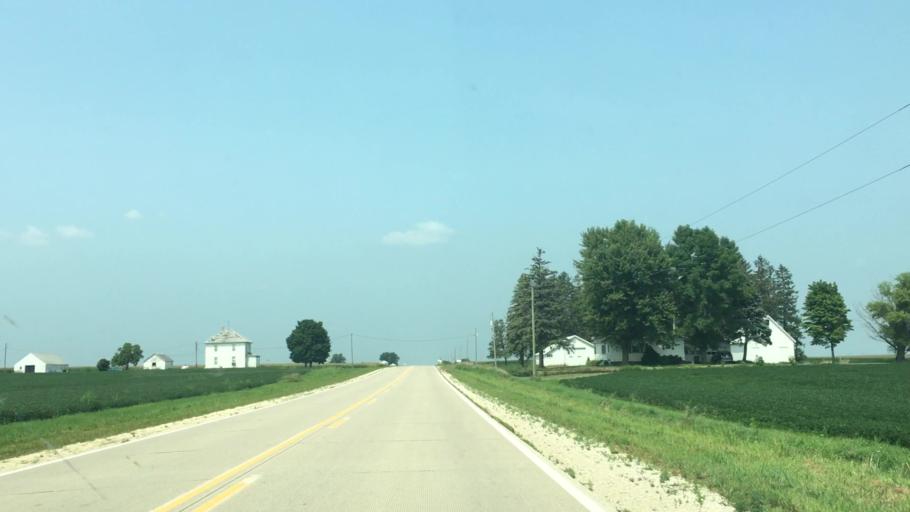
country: US
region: Iowa
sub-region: Fayette County
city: Oelwein
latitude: 42.7095
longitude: -91.8048
